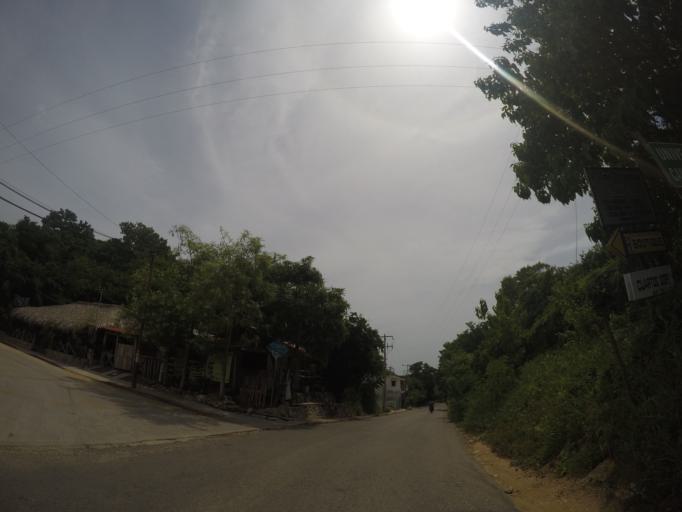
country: MX
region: Oaxaca
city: San Pedro Pochutla
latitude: 15.6644
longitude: -96.5020
